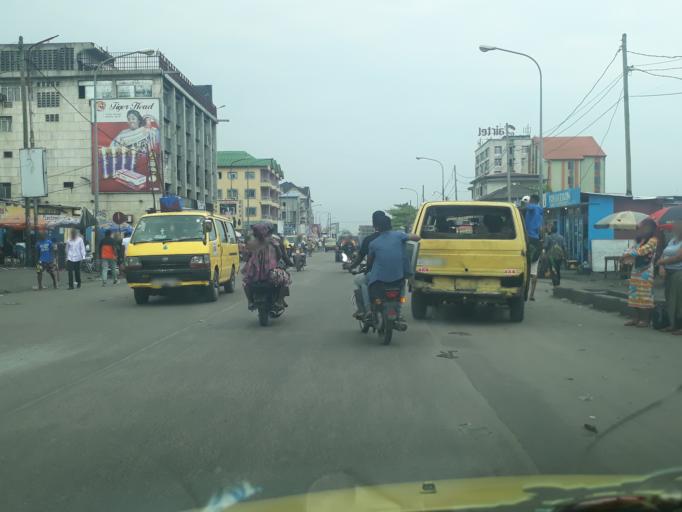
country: CD
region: Kinshasa
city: Kinshasa
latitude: -4.3435
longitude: 15.3129
